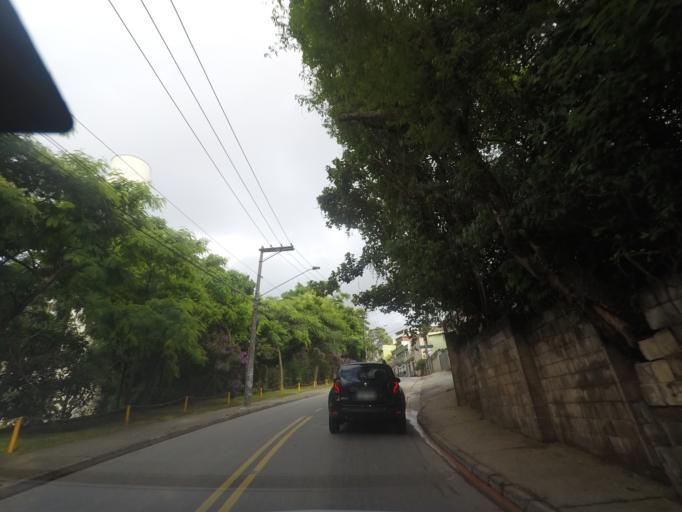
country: BR
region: Sao Paulo
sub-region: Taboao Da Serra
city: Taboao da Serra
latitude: -23.5813
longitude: -46.7767
